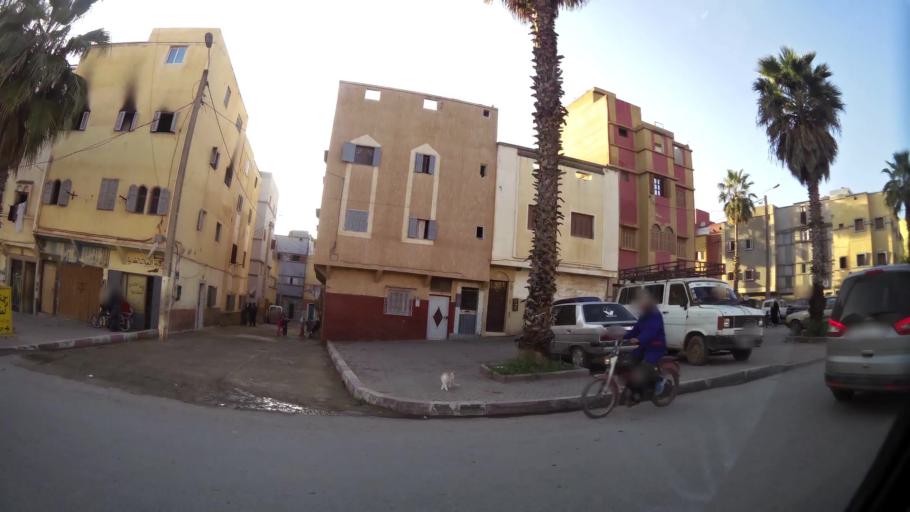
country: MA
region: Chaouia-Ouardigha
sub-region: Settat Province
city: Settat
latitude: 32.9971
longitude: -7.6040
